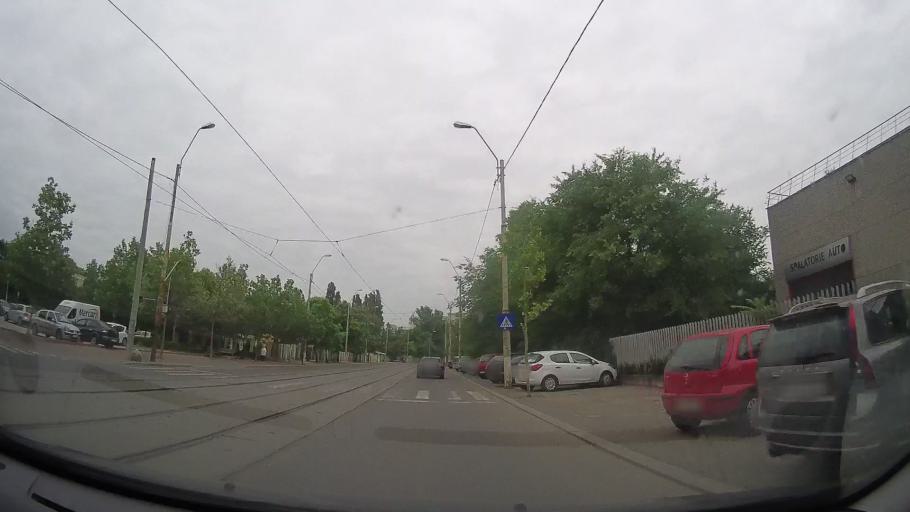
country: RO
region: Ilfov
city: Dobroesti
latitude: 44.4328
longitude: 26.1726
